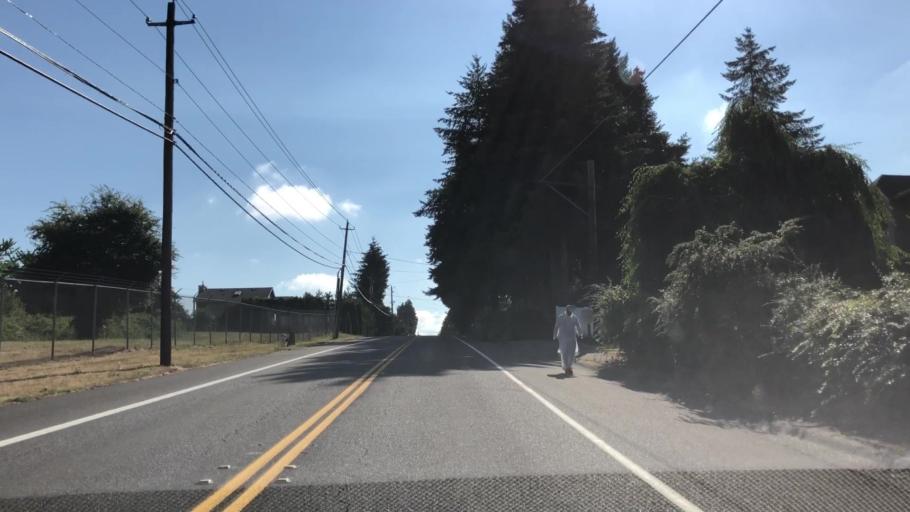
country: US
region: Washington
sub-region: King County
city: East Hill-Meridian
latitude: 47.4231
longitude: -122.2041
